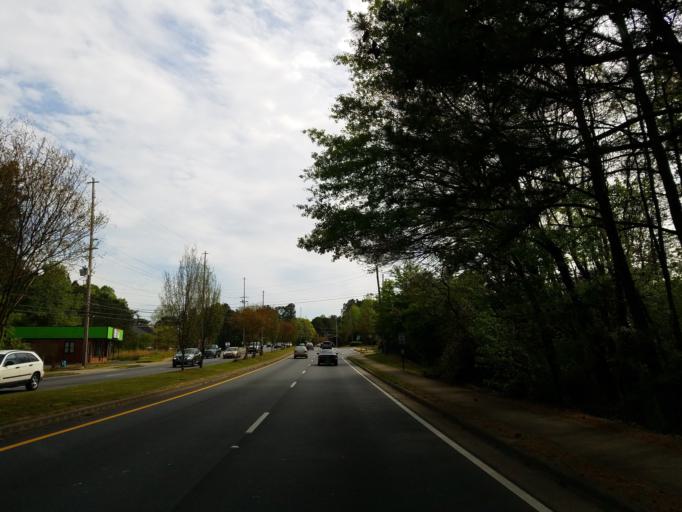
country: US
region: Georgia
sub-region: Cobb County
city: Mableton
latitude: 33.8716
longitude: -84.5911
